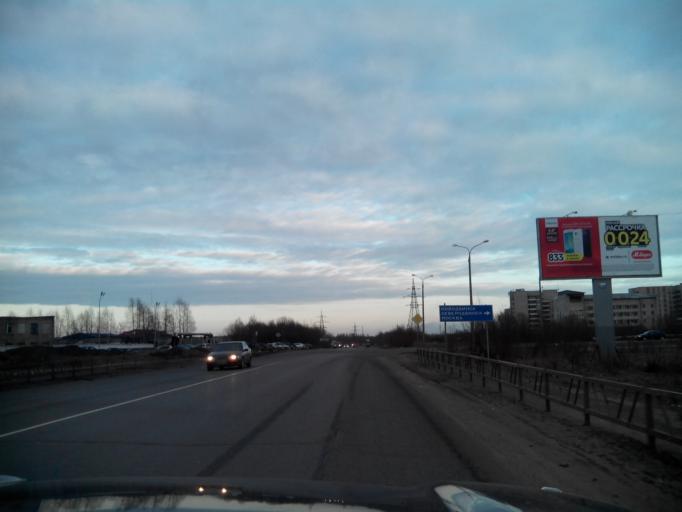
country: RU
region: Arkhangelskaya
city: Arkhangel'sk
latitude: 64.5188
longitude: 40.6768
